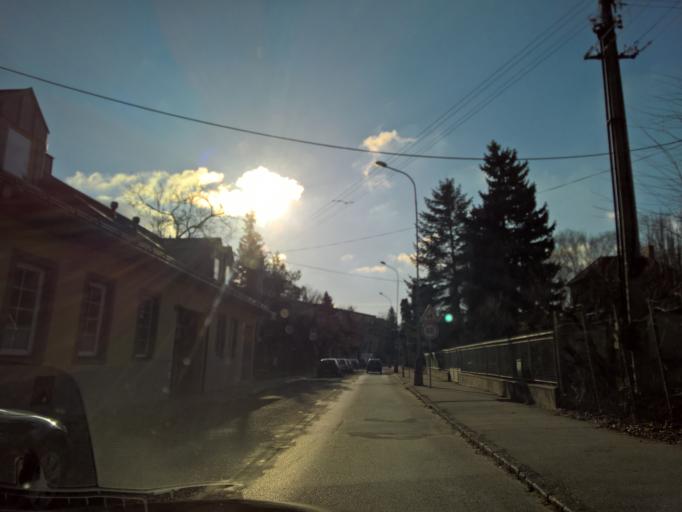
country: SK
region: Nitriansky
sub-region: Okres Nitra
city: Nitra
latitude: 48.3127
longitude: 18.0791
